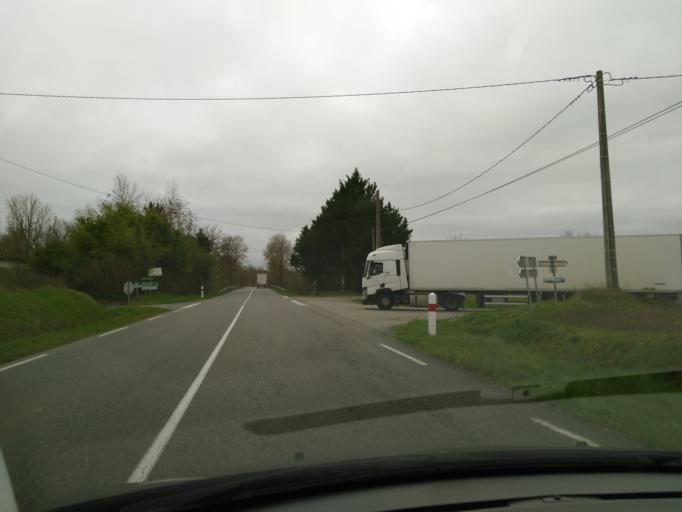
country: FR
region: Aquitaine
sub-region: Departement du Lot-et-Garonne
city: Castillonnes
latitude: 44.6745
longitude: 0.5788
